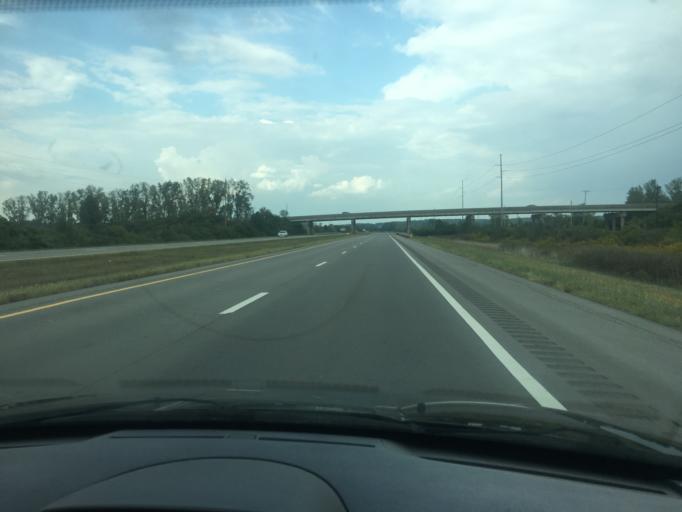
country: US
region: Ohio
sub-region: Clark County
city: Springfield
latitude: 39.9564
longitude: -83.8283
